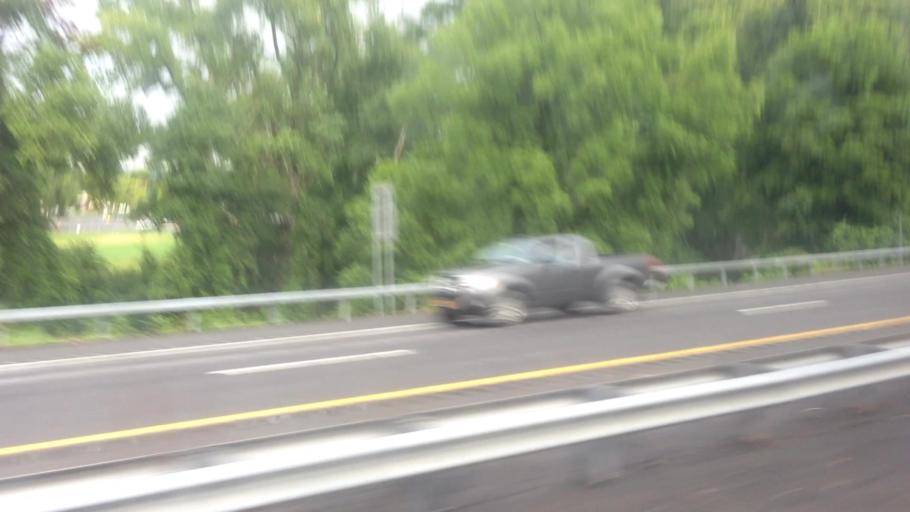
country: US
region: New York
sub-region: Ulster County
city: Kingston
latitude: 41.9355
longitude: -74.0118
